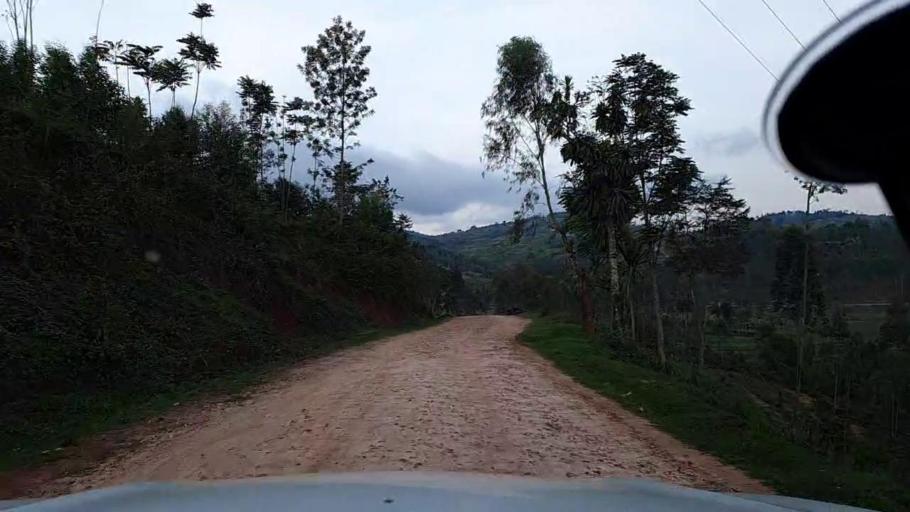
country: RW
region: Southern Province
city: Nyanza
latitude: -2.2109
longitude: 29.6120
